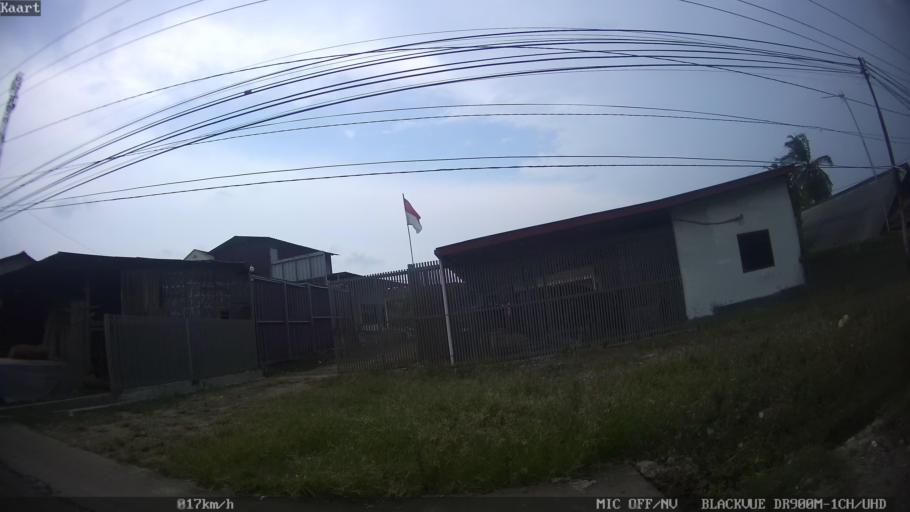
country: ID
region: Lampung
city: Bandarlampung
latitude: -5.4117
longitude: 105.2878
